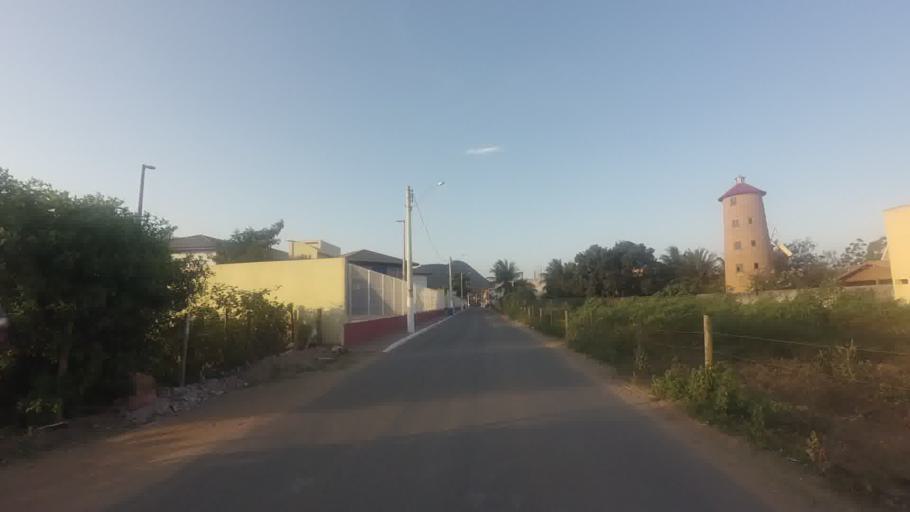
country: BR
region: Espirito Santo
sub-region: Piuma
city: Piuma
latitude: -20.8917
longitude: -40.7827
